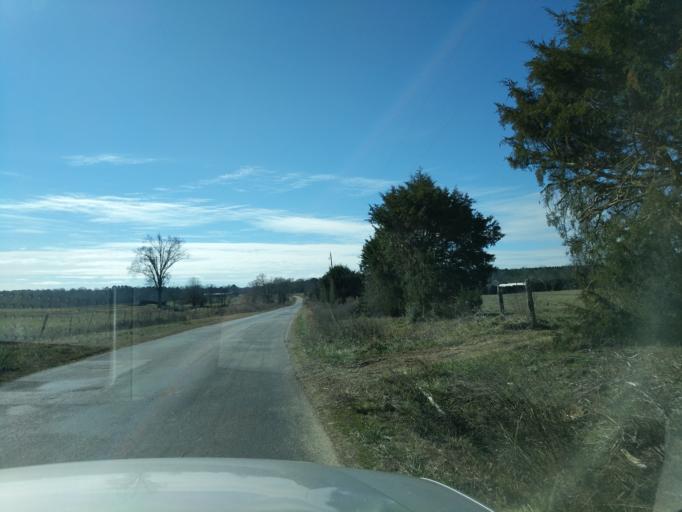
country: US
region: South Carolina
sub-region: Saluda County
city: Saluda
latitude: 34.0138
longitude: -81.8470
